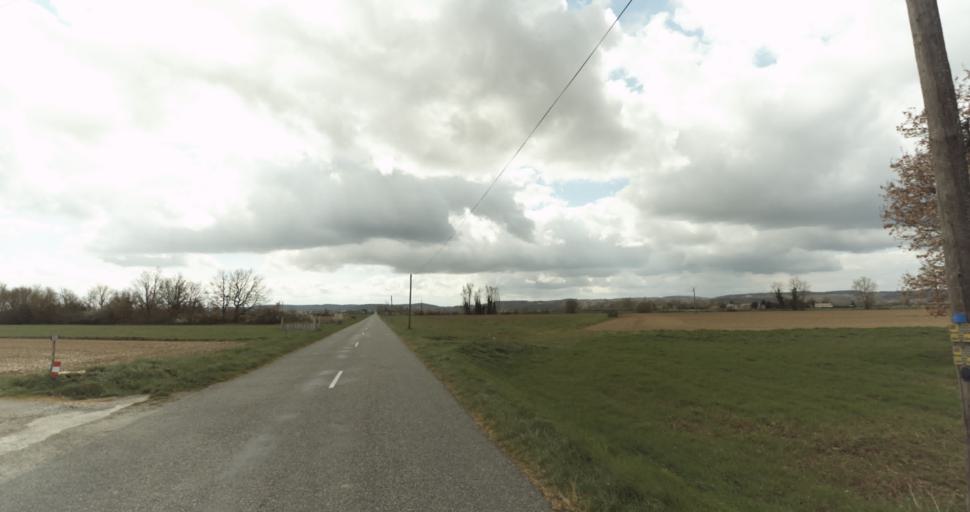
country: FR
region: Midi-Pyrenees
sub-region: Departement de la Haute-Garonne
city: Auterive
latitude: 43.3317
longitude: 1.4784
